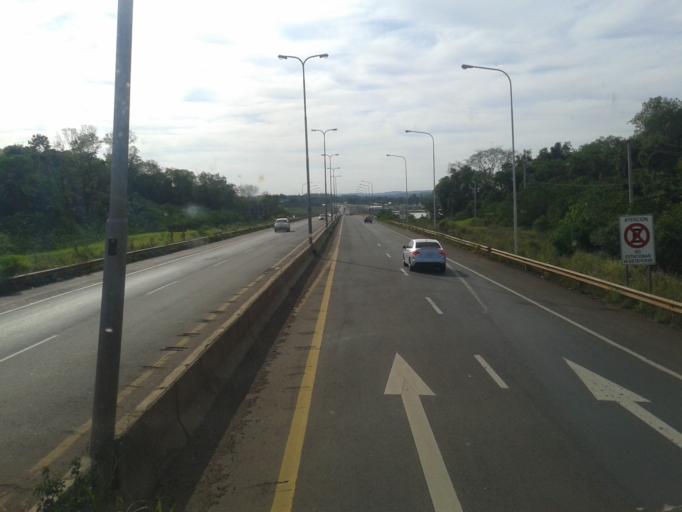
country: AR
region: Misiones
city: Garupa
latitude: -27.4616
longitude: -55.8200
